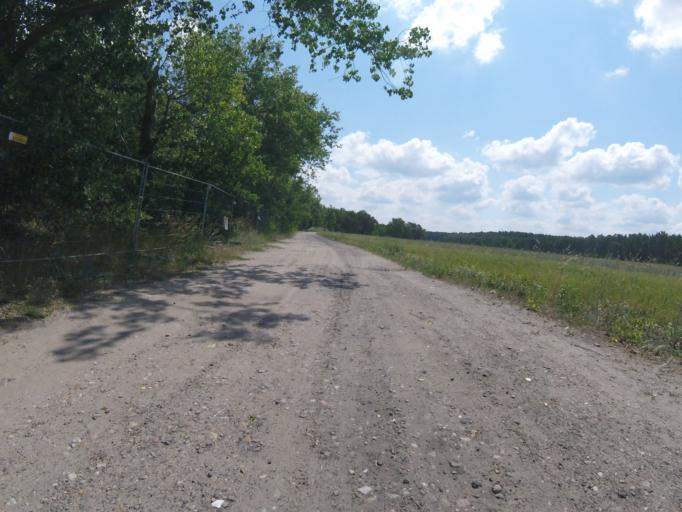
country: DE
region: Brandenburg
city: Bestensee
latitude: 52.2834
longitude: 13.6733
